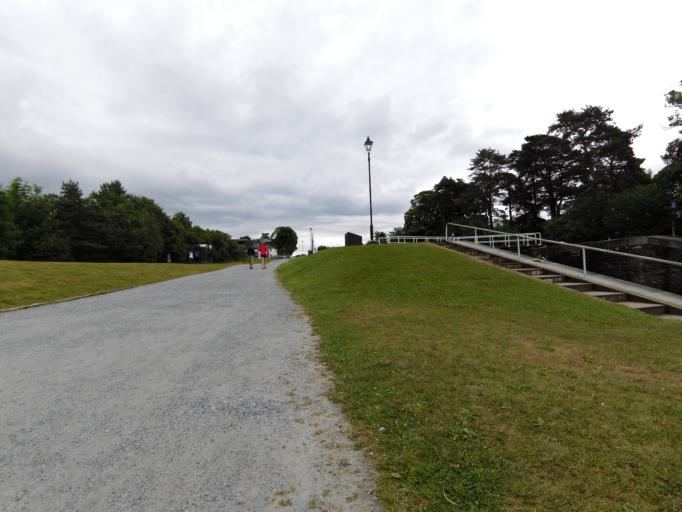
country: GB
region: Scotland
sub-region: Highland
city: Fort William
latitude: 56.8450
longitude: -5.0963
